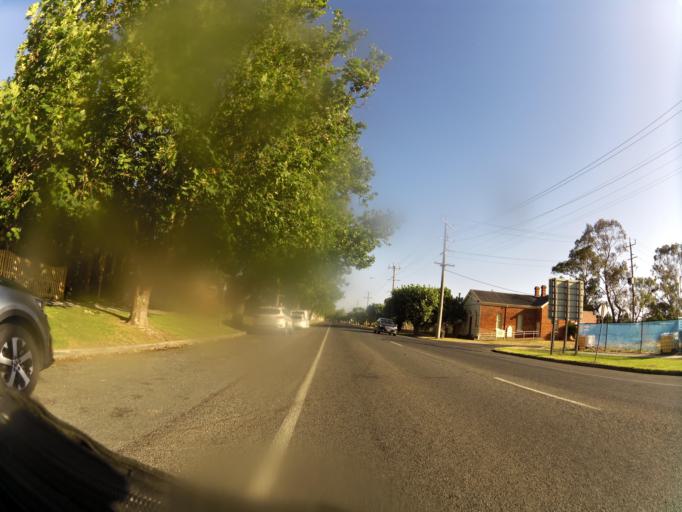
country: AU
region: Victoria
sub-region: Murrindindi
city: Kinglake West
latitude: -37.0200
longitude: 145.1296
